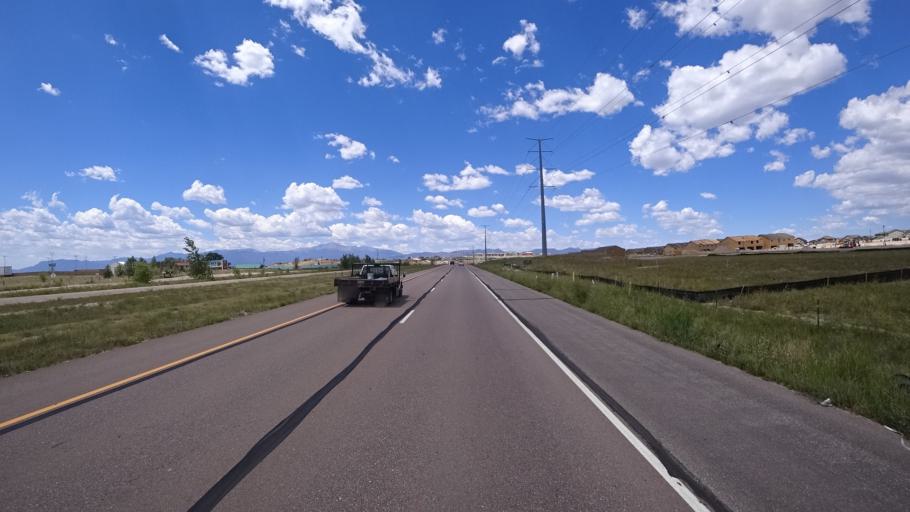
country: US
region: Colorado
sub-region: El Paso County
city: Black Forest
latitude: 38.9414
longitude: -104.6876
